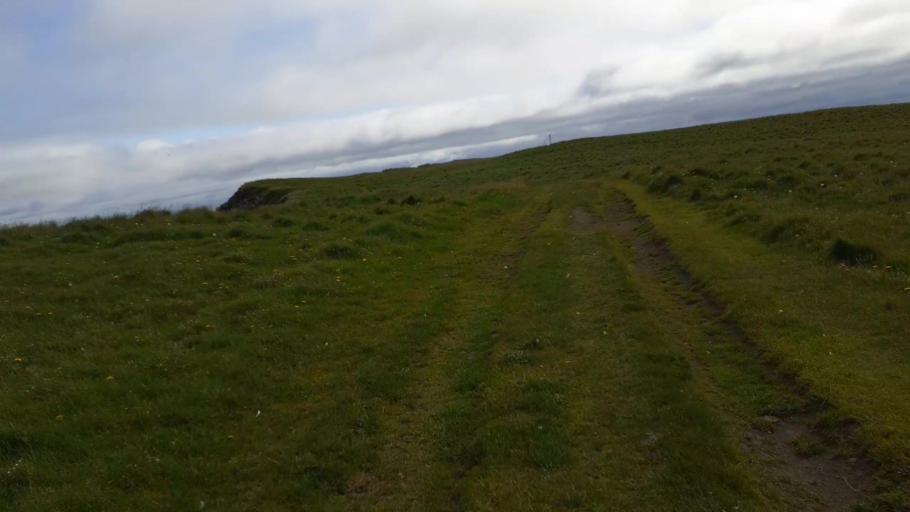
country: IS
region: Northeast
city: Dalvik
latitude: 66.5550
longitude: -18.0017
